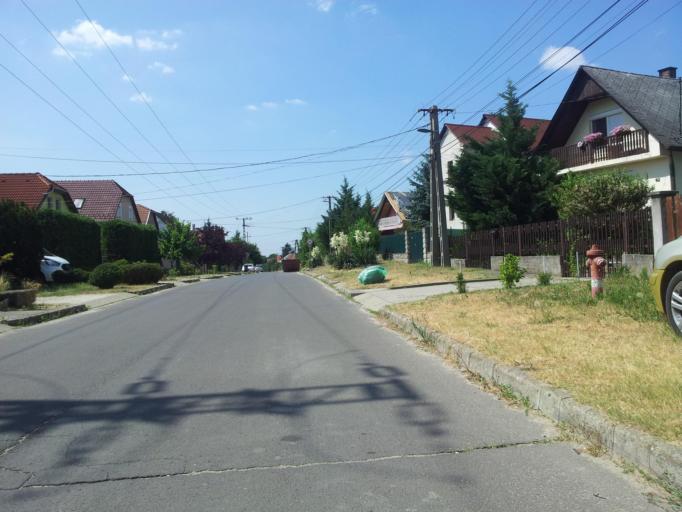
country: HU
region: Pest
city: Veresegyhaz
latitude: 47.6477
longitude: 19.2995
